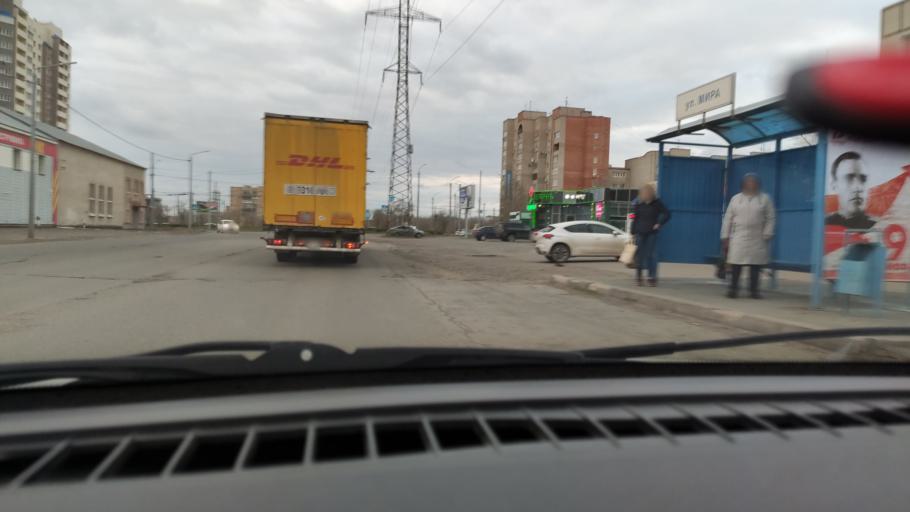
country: RU
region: Orenburg
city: Orenburg
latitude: 51.7859
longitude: 55.1719
